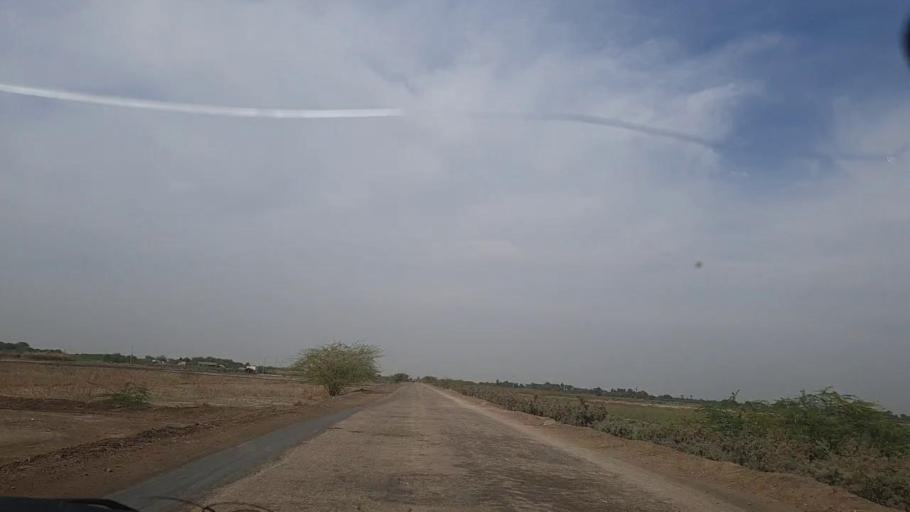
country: PK
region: Sindh
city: Pithoro
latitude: 25.5369
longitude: 69.3606
